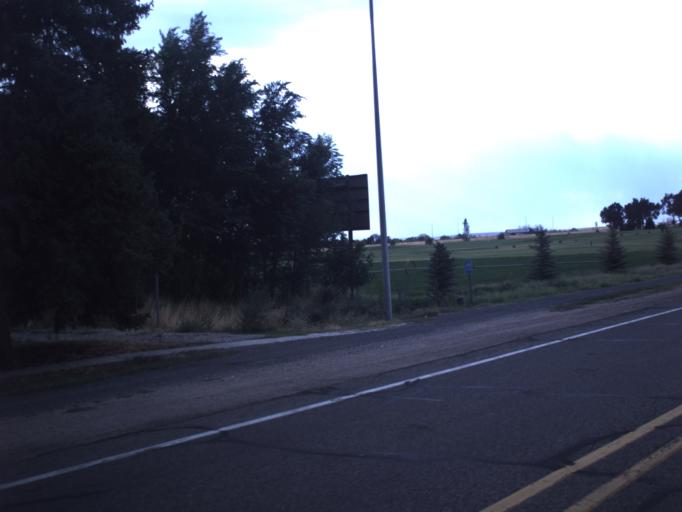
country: US
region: Utah
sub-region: Millard County
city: Fillmore
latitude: 38.9833
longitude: -112.3237
